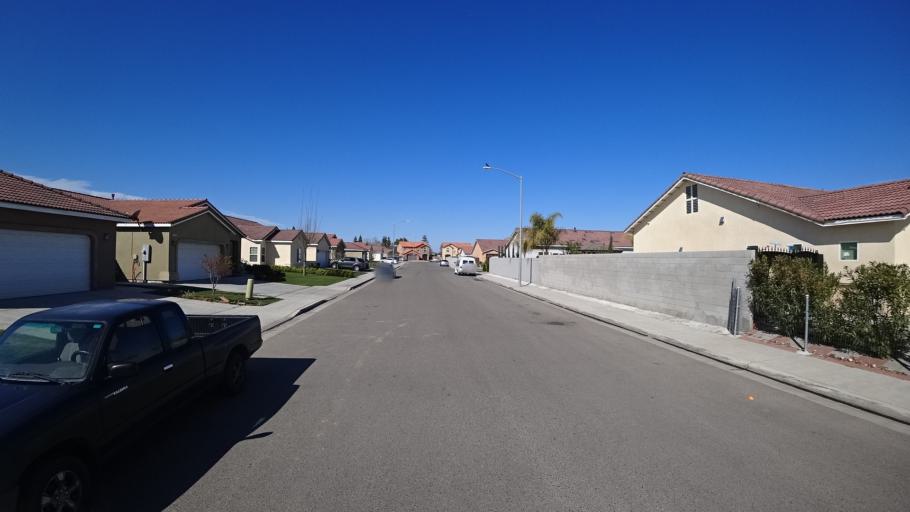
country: US
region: California
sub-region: Fresno County
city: West Park
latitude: 36.8030
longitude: -119.8856
